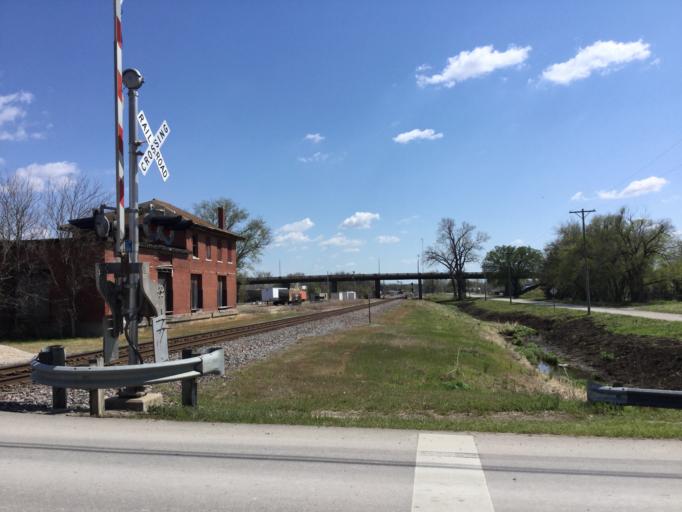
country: US
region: Kansas
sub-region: Montgomery County
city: Independence
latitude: 37.2255
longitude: -95.7243
